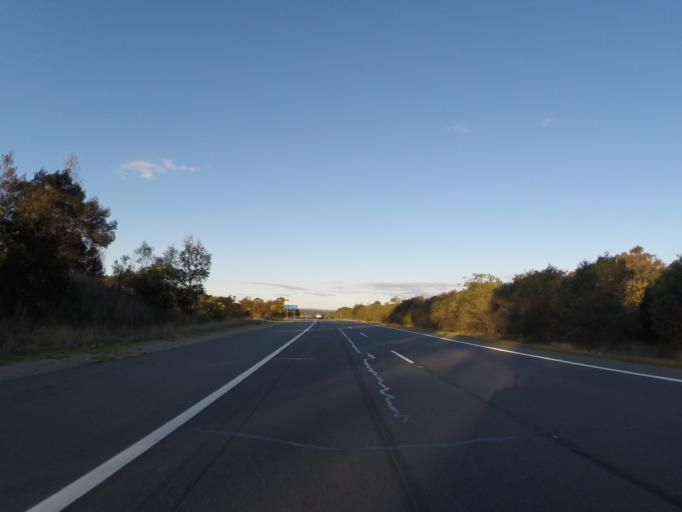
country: AU
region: Australian Capital Territory
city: Kaleen
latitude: -35.2053
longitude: 149.2010
